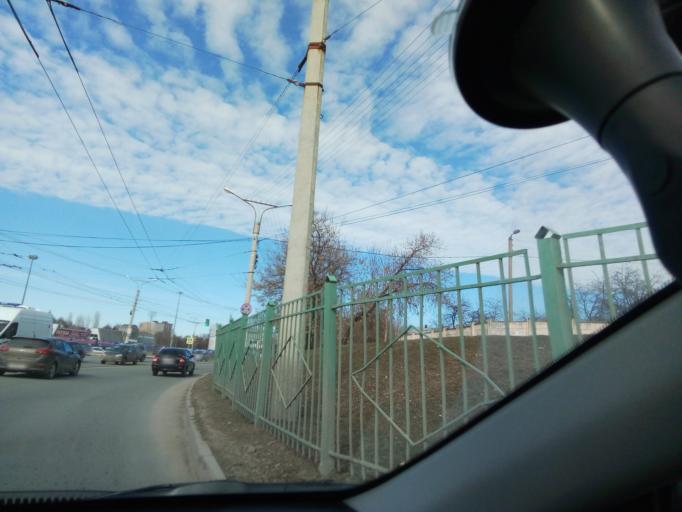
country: RU
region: Chuvashia
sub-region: Cheboksarskiy Rayon
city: Cheboksary
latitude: 56.1121
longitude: 47.2478
